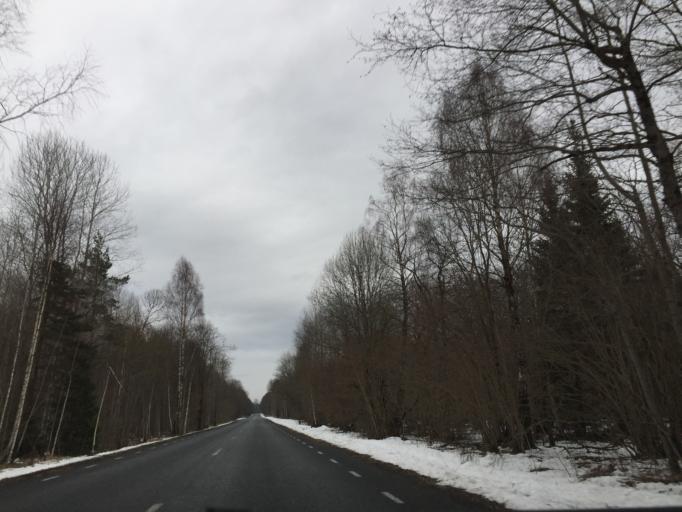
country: EE
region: Saare
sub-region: Orissaare vald
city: Orissaare
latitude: 58.5663
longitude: 22.7653
